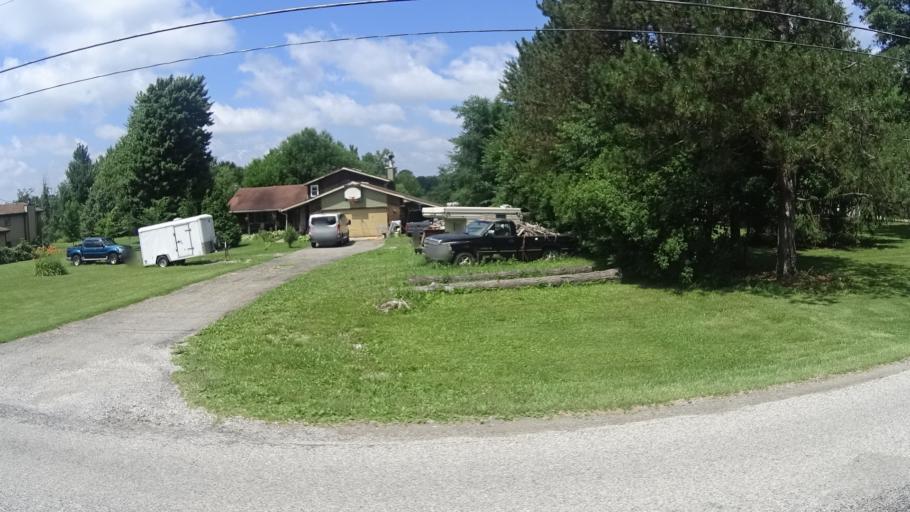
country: US
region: Ohio
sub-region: Huron County
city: Wakeman
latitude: 41.2848
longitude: -82.3625
